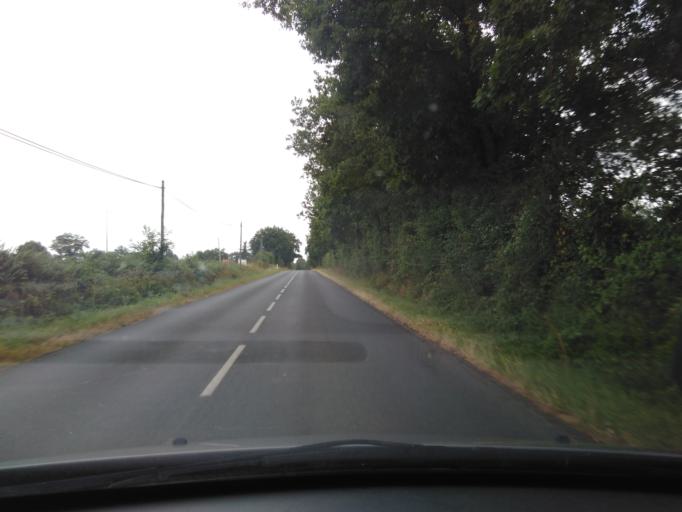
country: FR
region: Pays de la Loire
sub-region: Departement de la Vendee
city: Dompierre-sur-Yon
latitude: 46.7522
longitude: -1.3850
